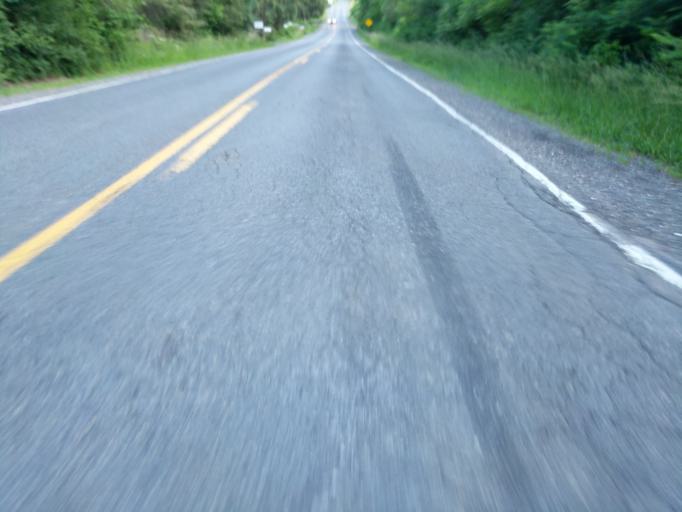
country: US
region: New York
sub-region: Tompkins County
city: Dryden
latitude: 42.3970
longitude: -76.3508
